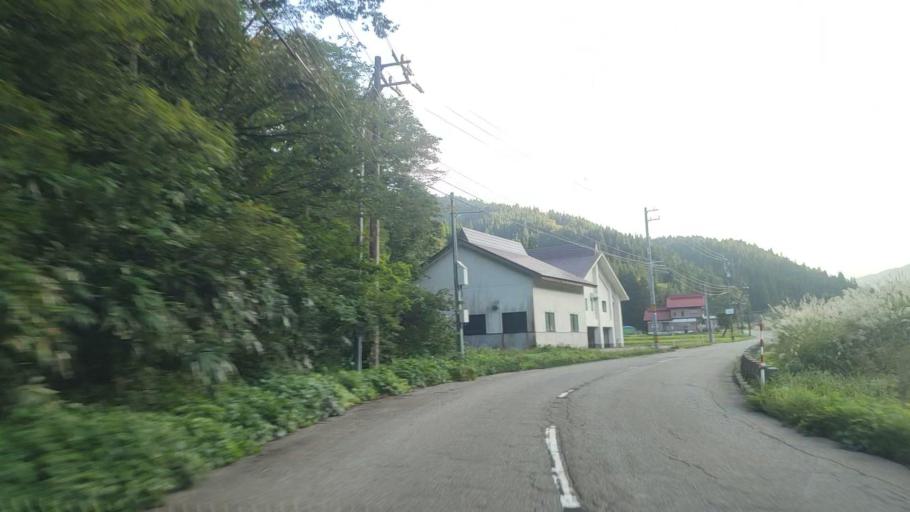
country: JP
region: Toyama
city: Yatsuomachi-higashikumisaka
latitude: 36.4697
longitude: 137.0486
